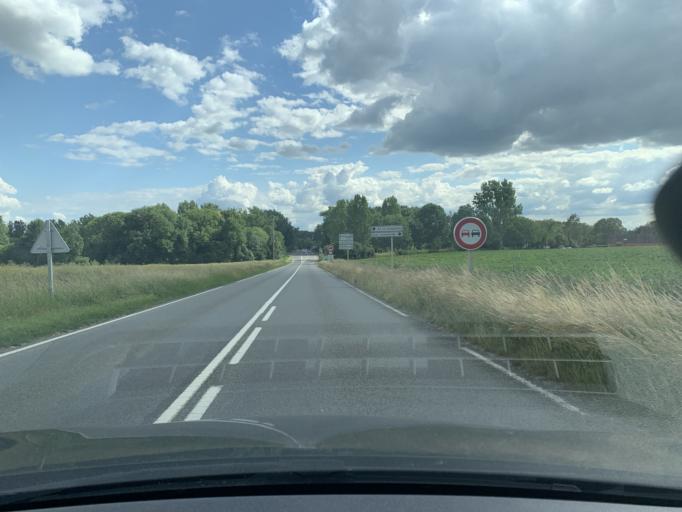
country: FR
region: Picardie
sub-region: Departement de la Somme
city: Peronne
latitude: 49.9398
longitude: 2.9493
